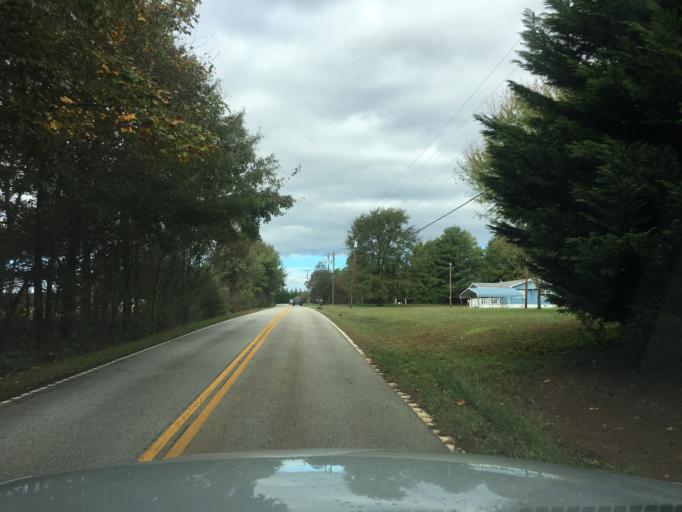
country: US
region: South Carolina
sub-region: Greenville County
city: Tigerville
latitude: 35.0562
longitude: -82.2580
